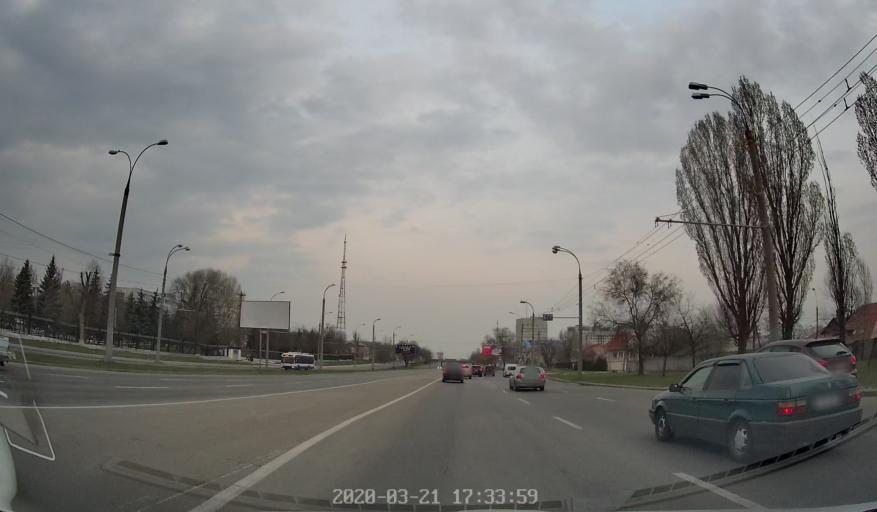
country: MD
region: Laloveni
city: Ialoveni
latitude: 46.9966
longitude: 28.8002
